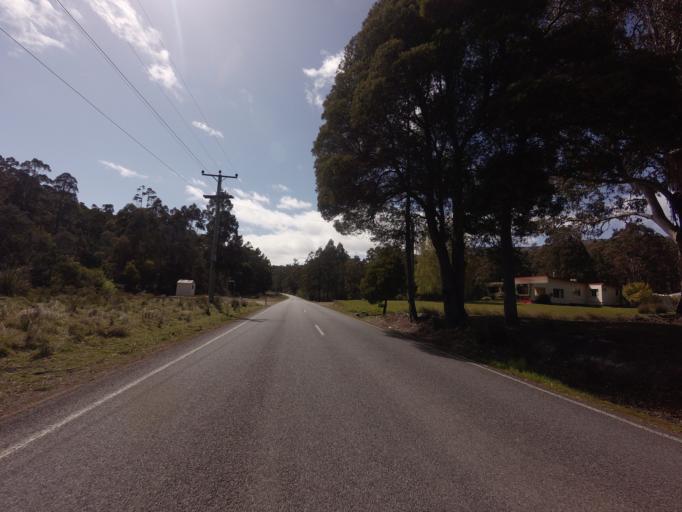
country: AU
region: Tasmania
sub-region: Derwent Valley
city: New Norfolk
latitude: -42.7179
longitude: 146.6881
